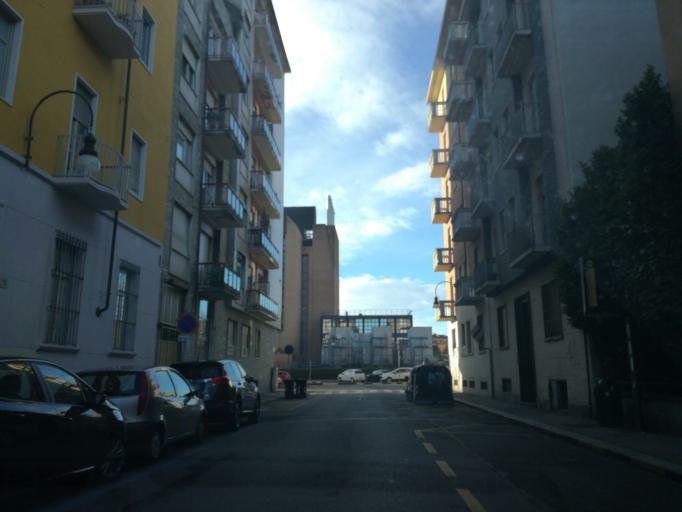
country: IT
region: Piedmont
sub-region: Provincia di Torino
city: Turin
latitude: 45.0730
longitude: 7.6571
